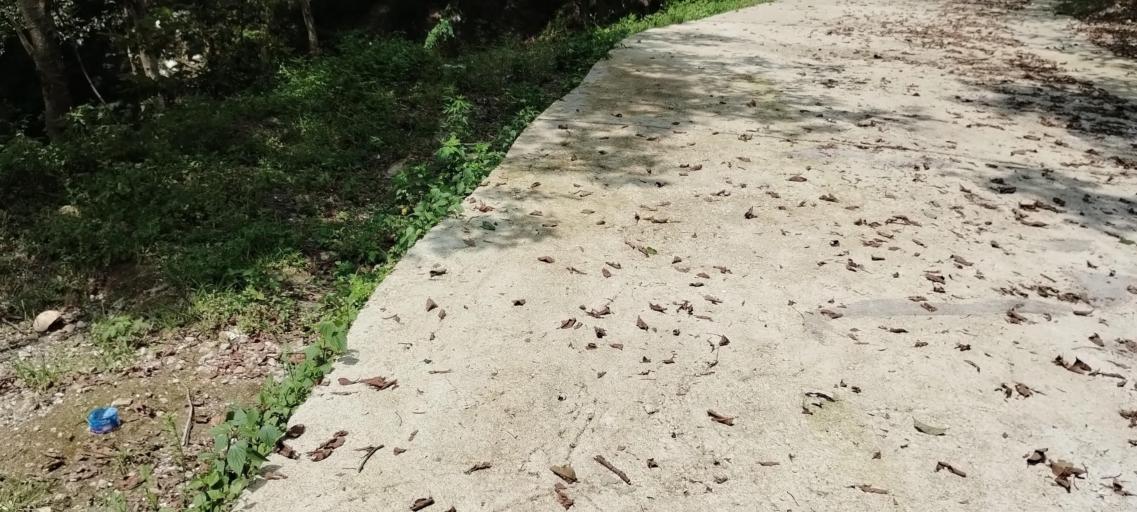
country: NP
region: Central Region
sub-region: Bagmati Zone
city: Kathmandu
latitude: 27.7914
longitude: 85.3625
